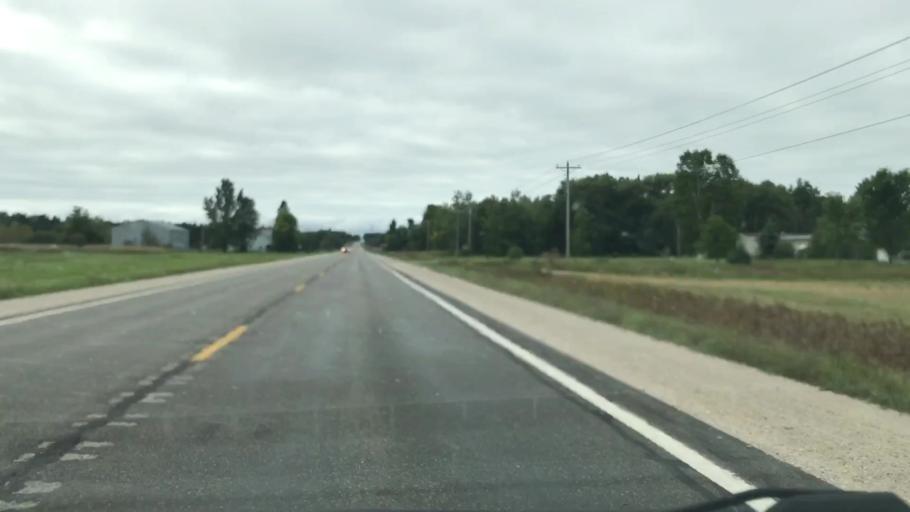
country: US
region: Michigan
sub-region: Luce County
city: Newberry
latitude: 46.1398
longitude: -85.5714
